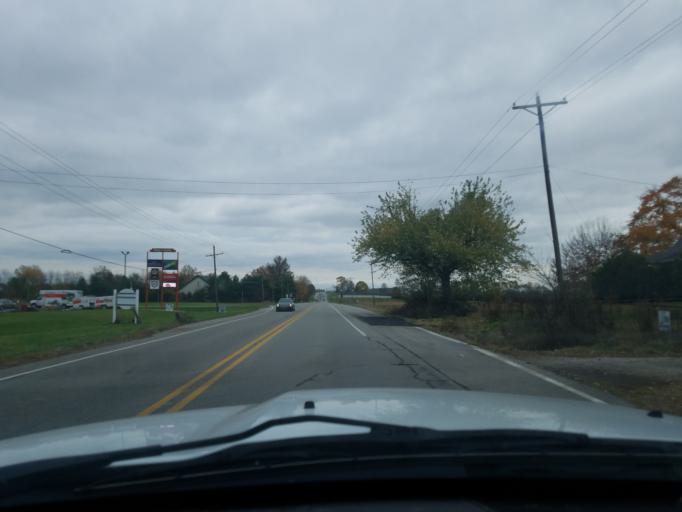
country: US
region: Indiana
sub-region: Bartholomew County
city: Hope
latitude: 39.2879
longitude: -85.7715
